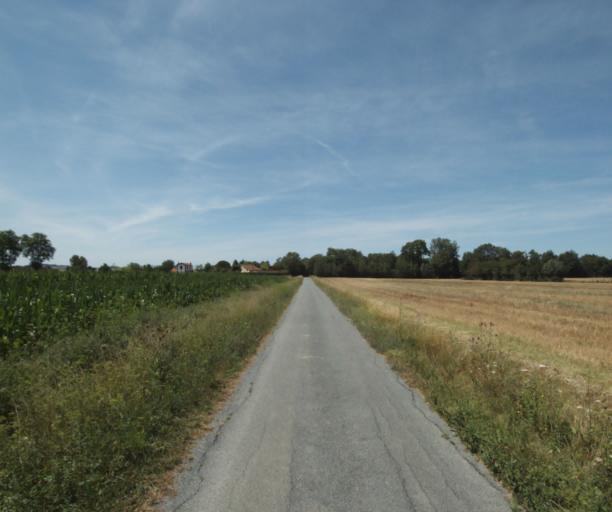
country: FR
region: Midi-Pyrenees
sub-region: Departement de la Haute-Garonne
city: Revel
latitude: 43.5109
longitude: 2.0131
